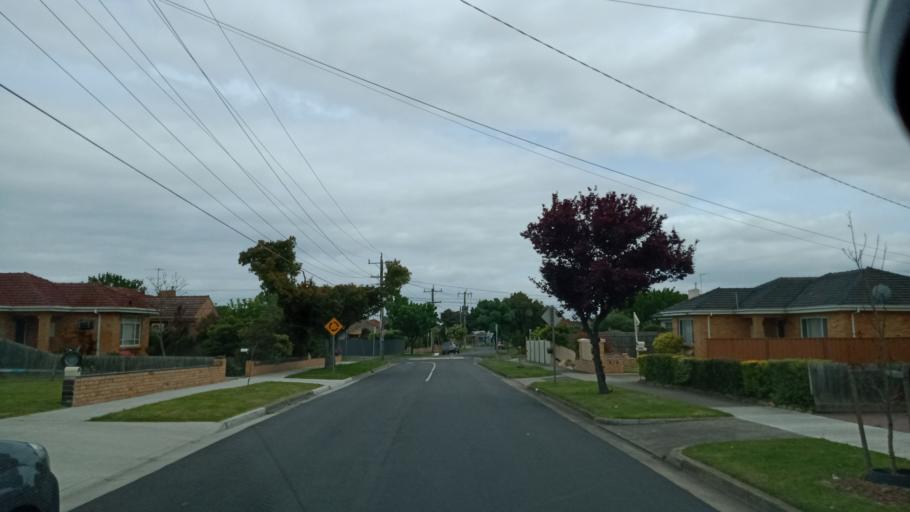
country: AU
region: Victoria
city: McKinnon
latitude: -37.9182
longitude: 145.0662
